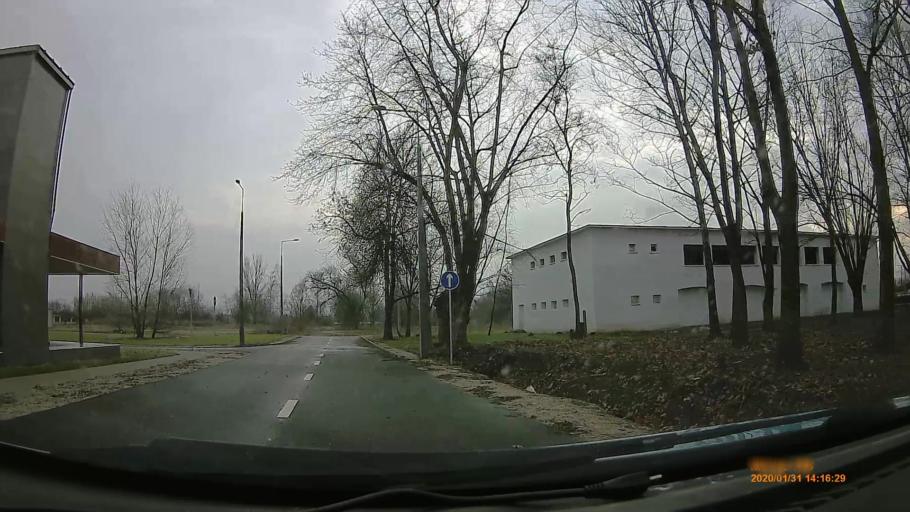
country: HU
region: Szabolcs-Szatmar-Bereg
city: Nyiregyhaza
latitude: 47.9564
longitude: 21.6790
